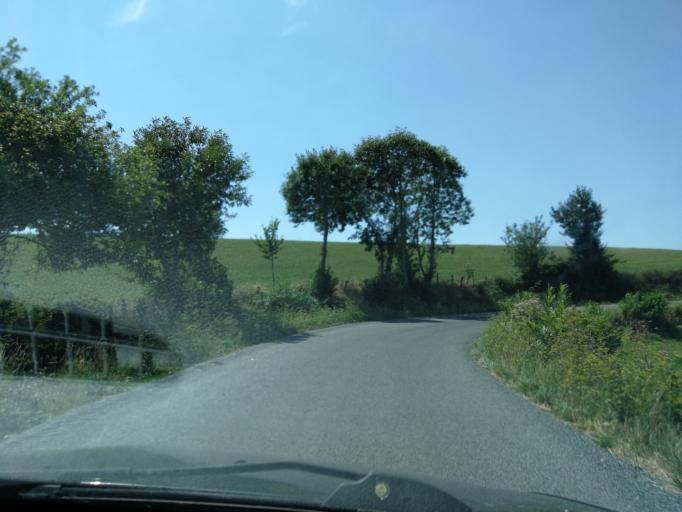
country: FR
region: Midi-Pyrenees
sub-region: Departement de l'Aveyron
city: Livinhac-le-Haut
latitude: 44.6624
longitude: 2.2777
